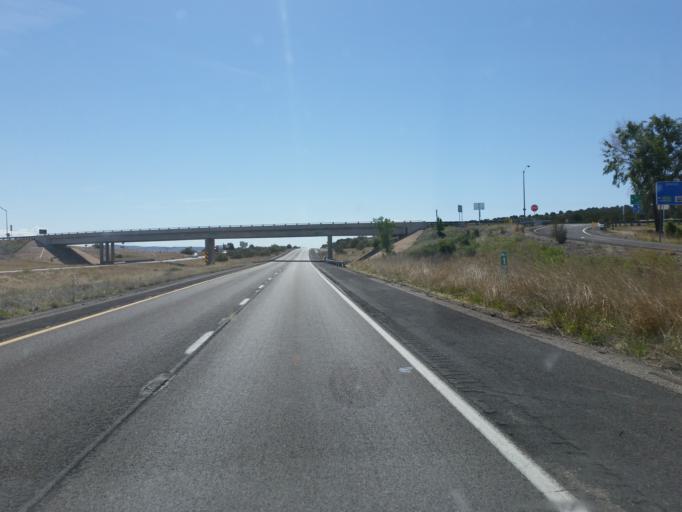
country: US
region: Arizona
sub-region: Mohave County
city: Peach Springs
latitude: 35.3203
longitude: -112.8949
